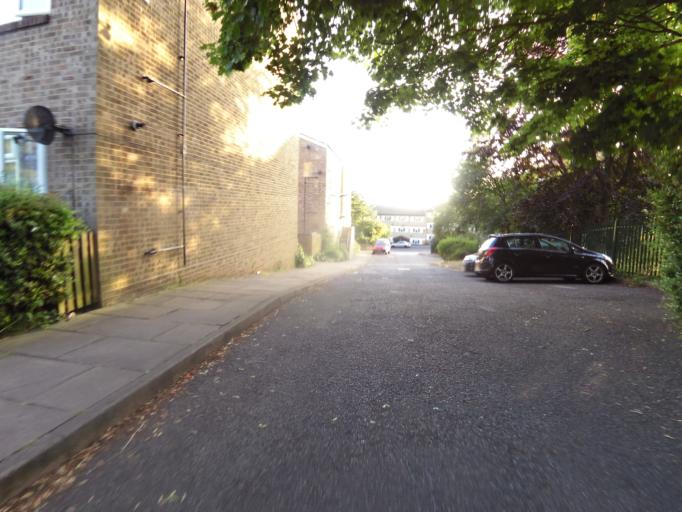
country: GB
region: England
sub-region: Suffolk
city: Ipswich
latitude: 52.0415
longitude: 1.1293
